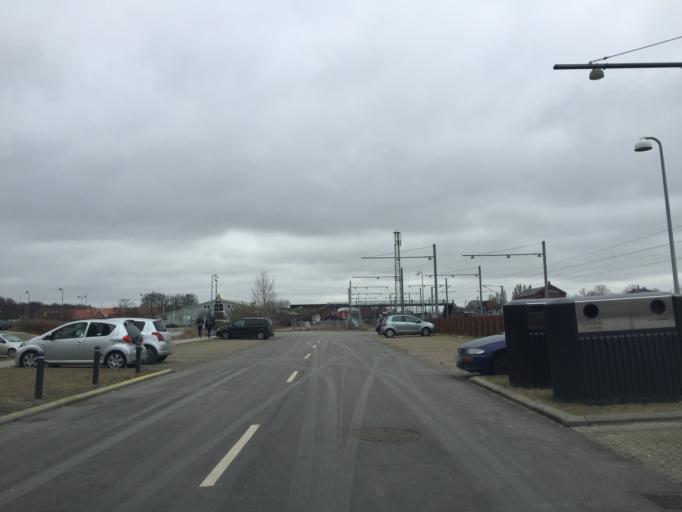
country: DK
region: Capital Region
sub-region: Hillerod Kommune
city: Hillerod
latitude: 55.9292
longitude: 12.3125
